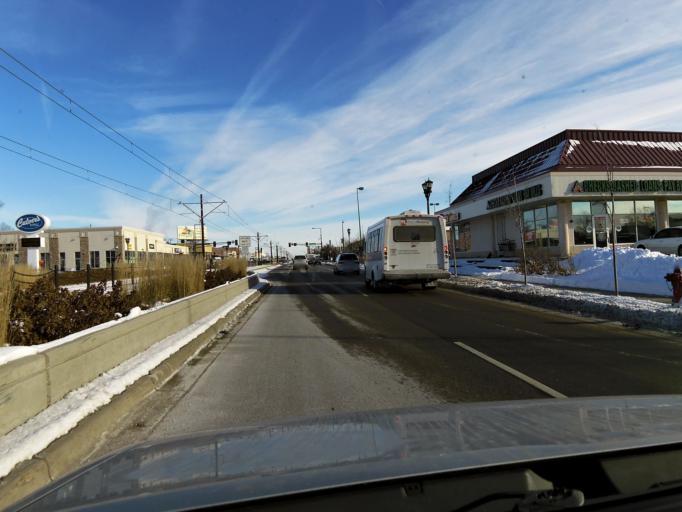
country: US
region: Minnesota
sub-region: Ramsey County
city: Falcon Heights
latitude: 44.9555
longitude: -93.1636
